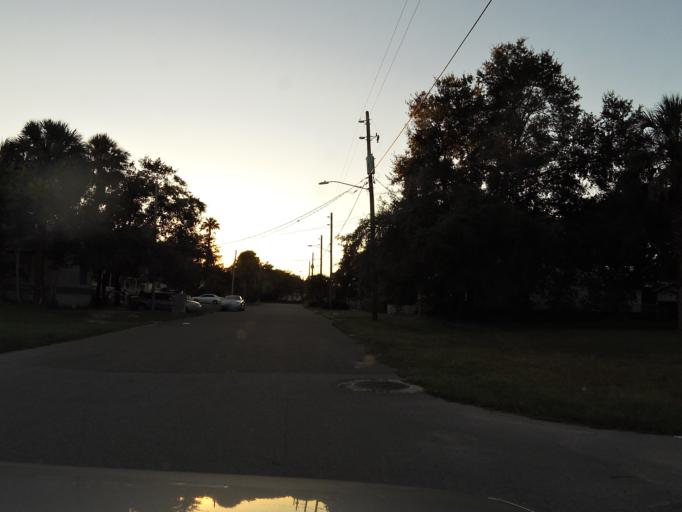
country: US
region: Florida
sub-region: Duval County
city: Jacksonville
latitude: 30.3336
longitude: -81.6456
